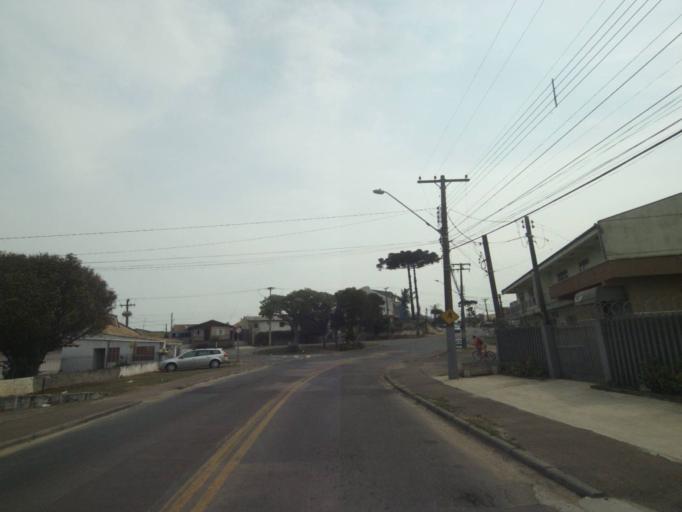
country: BR
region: Parana
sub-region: Sao Jose Dos Pinhais
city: Sao Jose dos Pinhais
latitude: -25.5217
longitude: -49.2841
